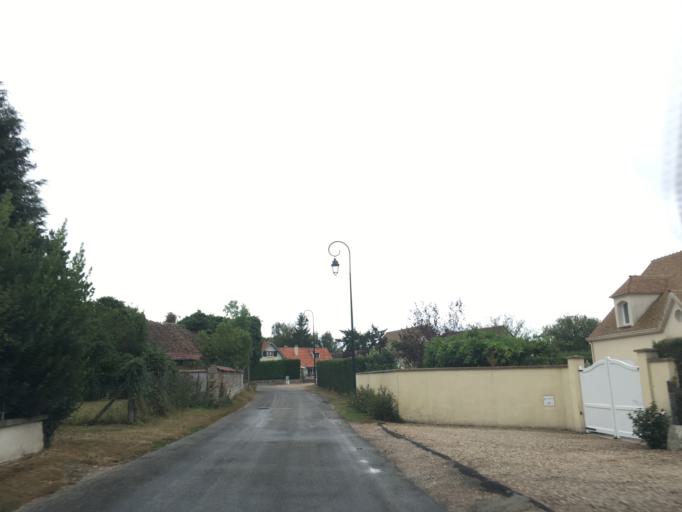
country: FR
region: Ile-de-France
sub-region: Departement des Yvelines
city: Limetz-Villez
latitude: 49.1027
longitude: 1.5367
